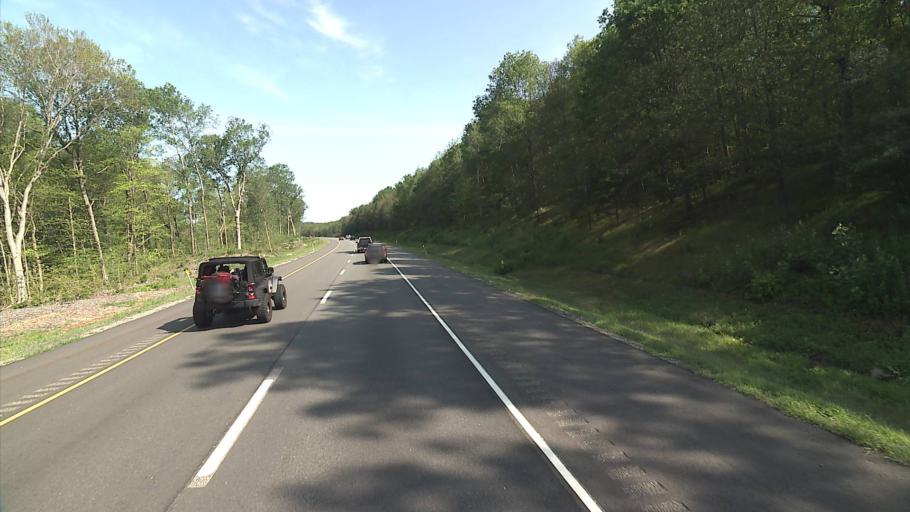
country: US
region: Connecticut
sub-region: Hartford County
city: Terramuggus
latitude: 41.6164
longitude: -72.4347
